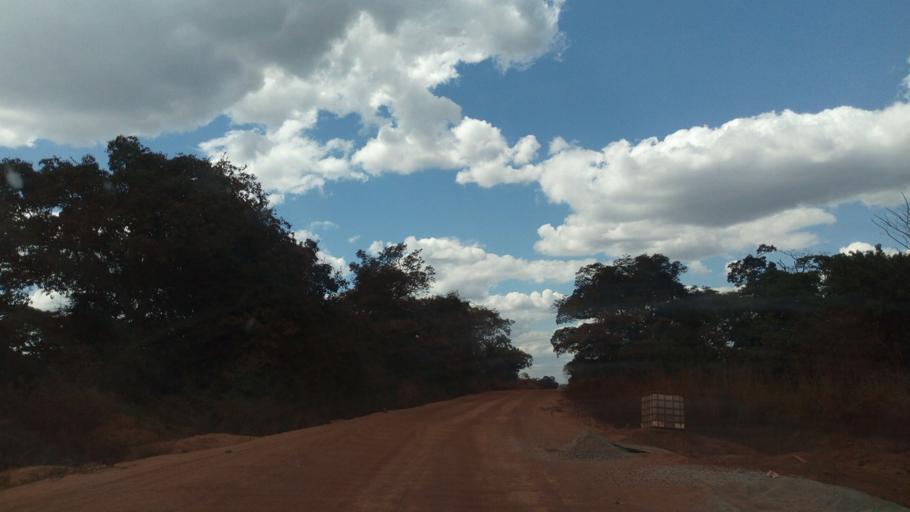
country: ZM
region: Copperbelt
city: Mufulira
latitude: -12.0294
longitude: 28.6737
